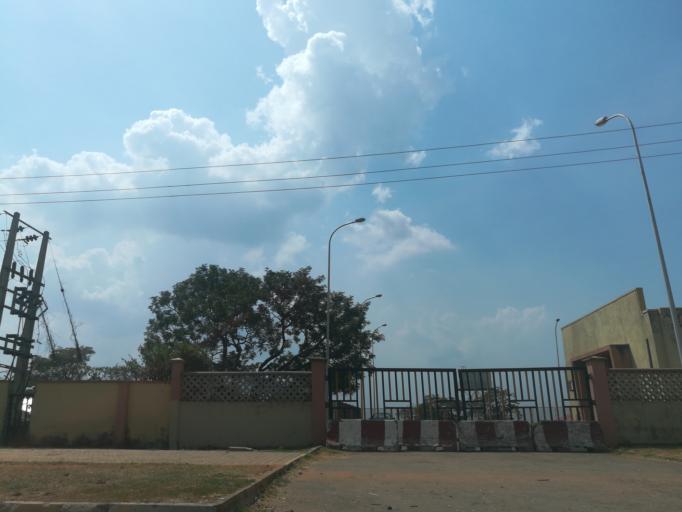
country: NG
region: Abuja Federal Capital Territory
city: Abuja
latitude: 9.0485
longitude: 7.4442
